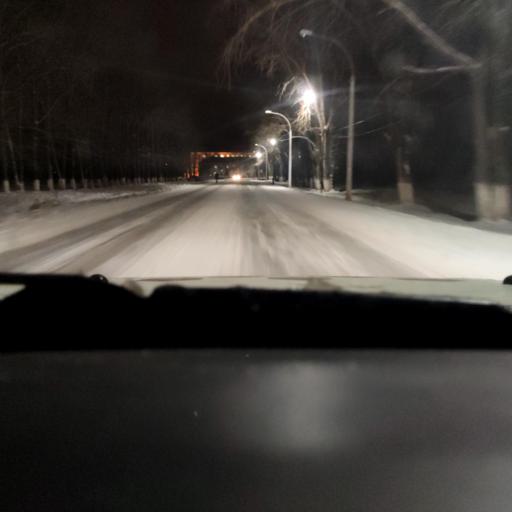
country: RU
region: Perm
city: Gamovo
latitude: 57.9120
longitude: 56.0424
